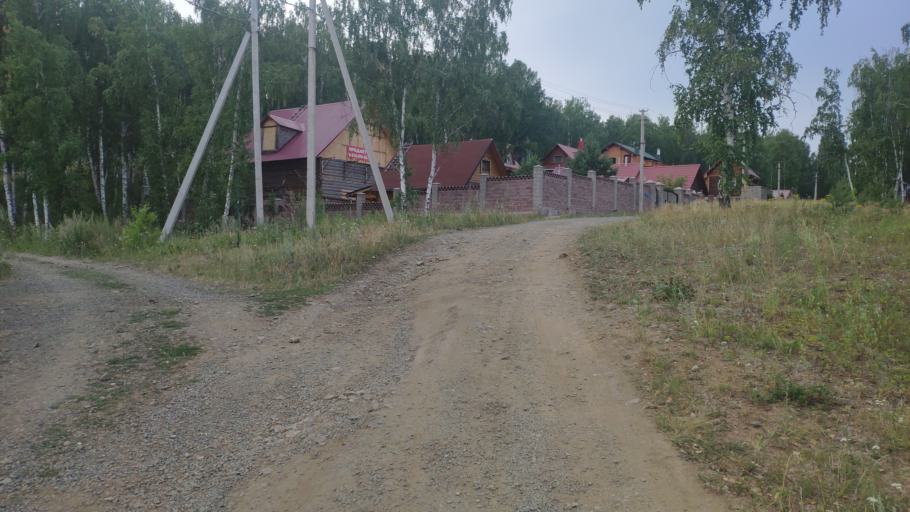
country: RU
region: Bashkortostan
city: Abzakovo
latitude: 53.8025
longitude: 58.6468
